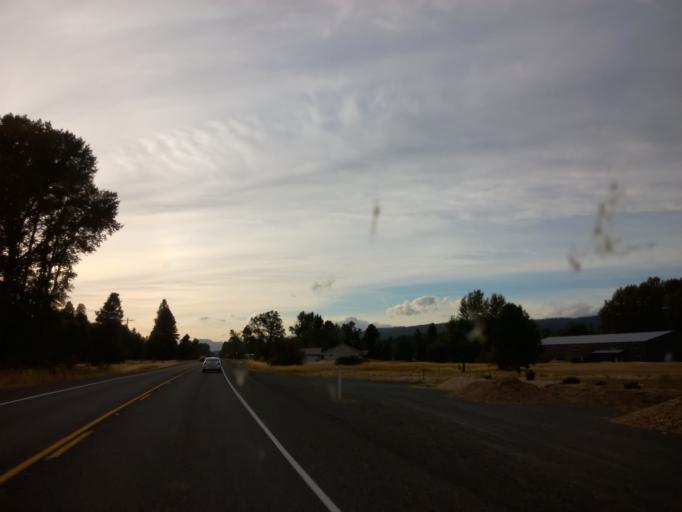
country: US
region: Washington
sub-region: Kittitas County
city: Cle Elum
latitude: 47.1755
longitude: -120.8589
